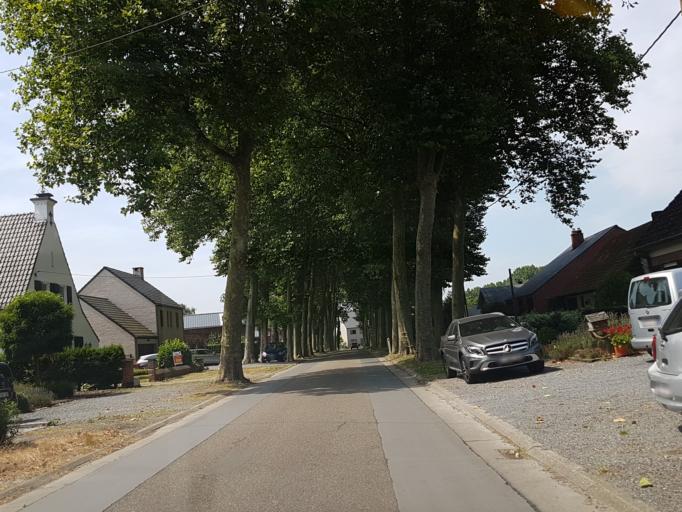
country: BE
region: Flanders
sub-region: Provincie Vlaams-Brabant
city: Kampenhout
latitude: 50.9401
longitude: 4.5675
